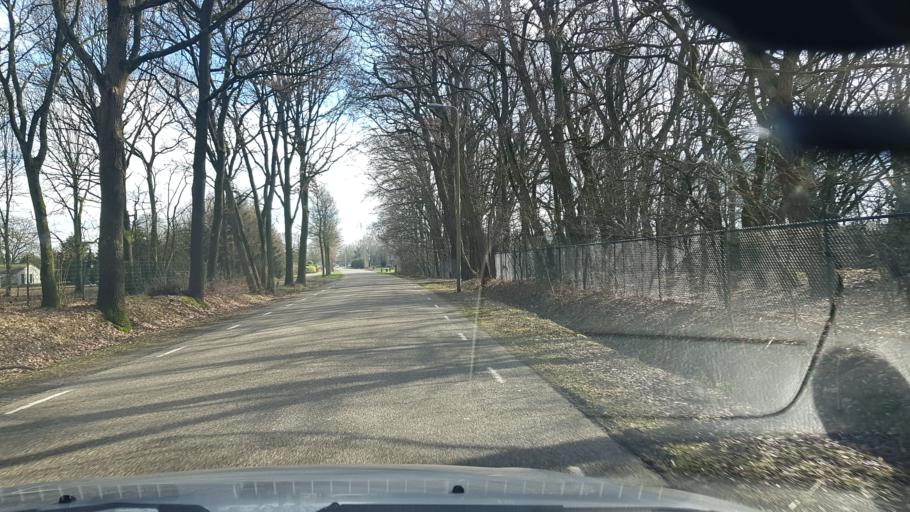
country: NL
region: Limburg
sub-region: Gemeente Nederweert
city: Nederweert
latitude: 51.2412
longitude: 5.7576
